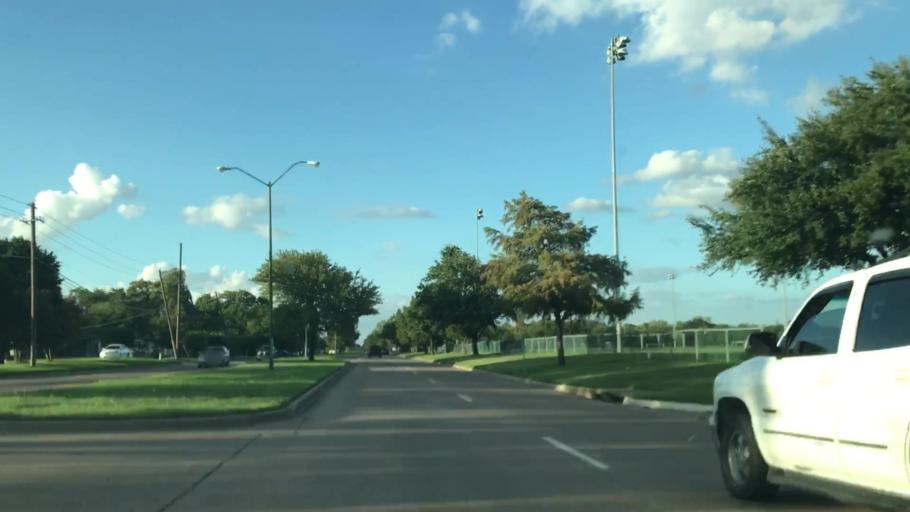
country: US
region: Texas
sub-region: Dallas County
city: Mesquite
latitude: 32.8120
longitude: -96.6653
